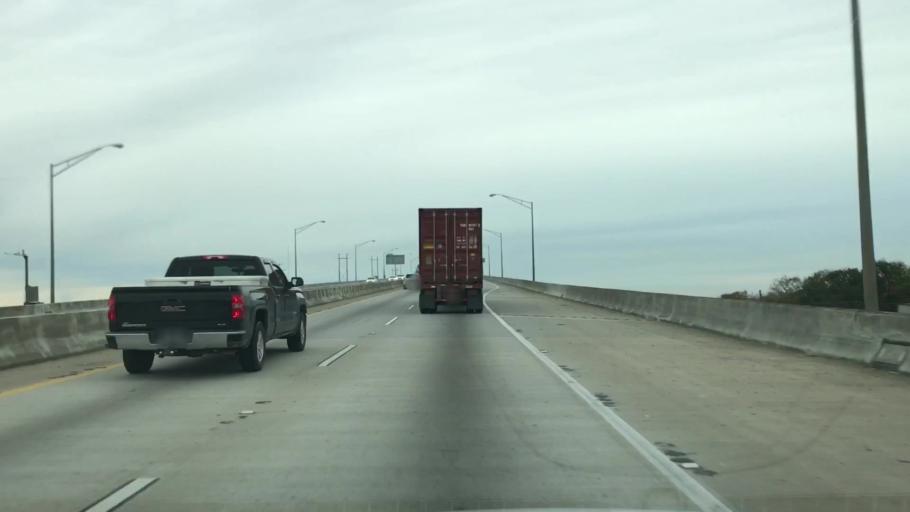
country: US
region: South Carolina
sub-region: Charleston County
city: North Charleston
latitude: 32.8927
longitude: -79.9743
